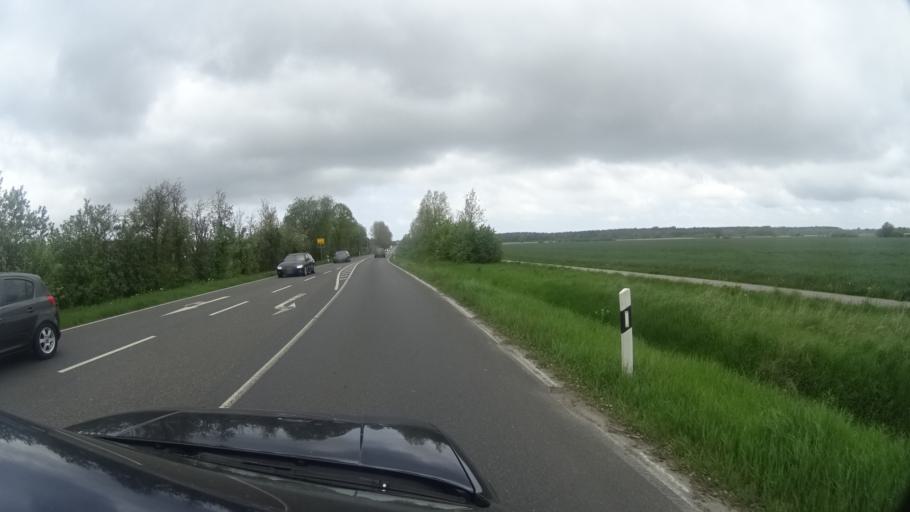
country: DE
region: Mecklenburg-Vorpommern
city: Ostseebad Dierhagen
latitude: 54.2428
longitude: 12.3614
